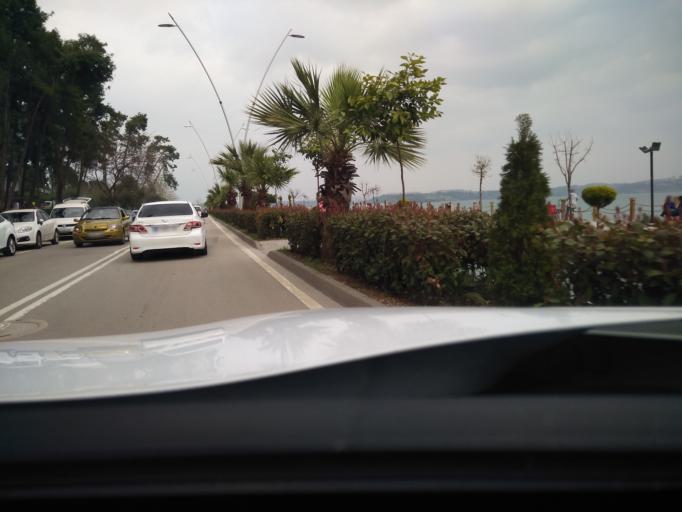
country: TR
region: Adana
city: Adana
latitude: 37.0552
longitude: 35.3064
